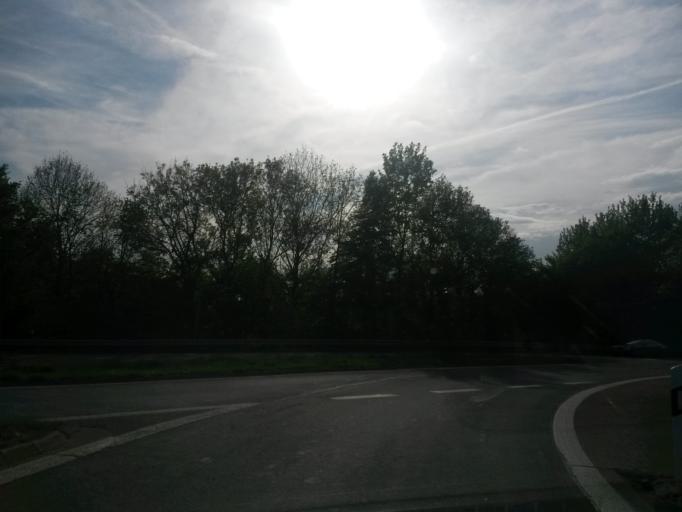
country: DE
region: North Rhine-Westphalia
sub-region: Regierungsbezirk Arnsberg
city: Luedenscheid
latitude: 51.2584
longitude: 7.6053
